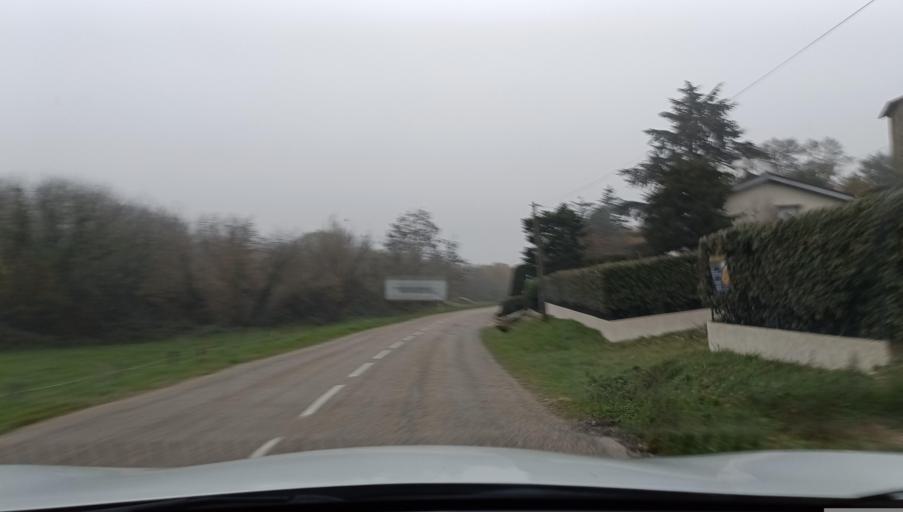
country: FR
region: Rhone-Alpes
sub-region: Departement de l'Isere
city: Serpaize
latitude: 45.5626
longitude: 4.9146
